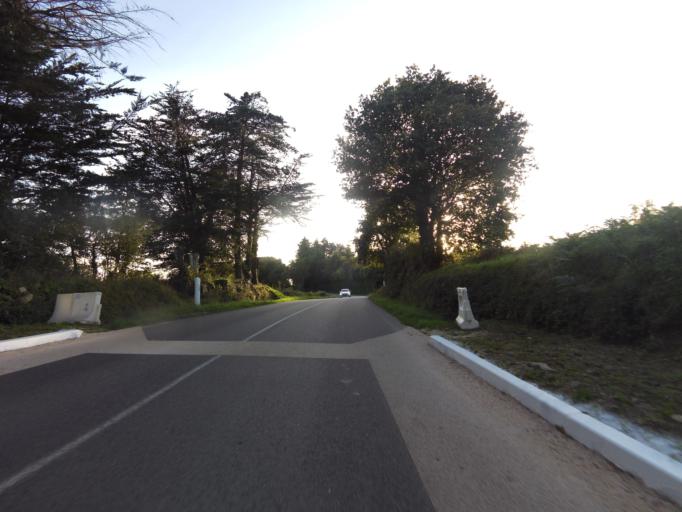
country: FR
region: Brittany
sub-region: Departement du Morbihan
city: Trefflean
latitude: 47.6385
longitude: -2.6021
